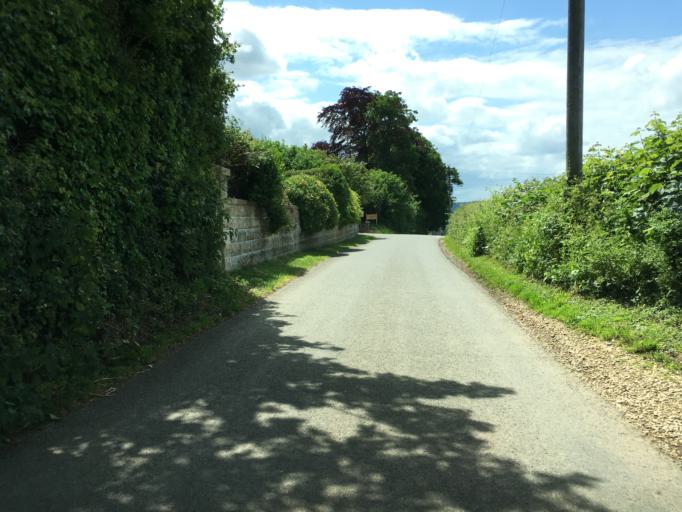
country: GB
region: England
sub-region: Gloucestershire
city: Stroud
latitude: 51.7592
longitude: -2.2142
